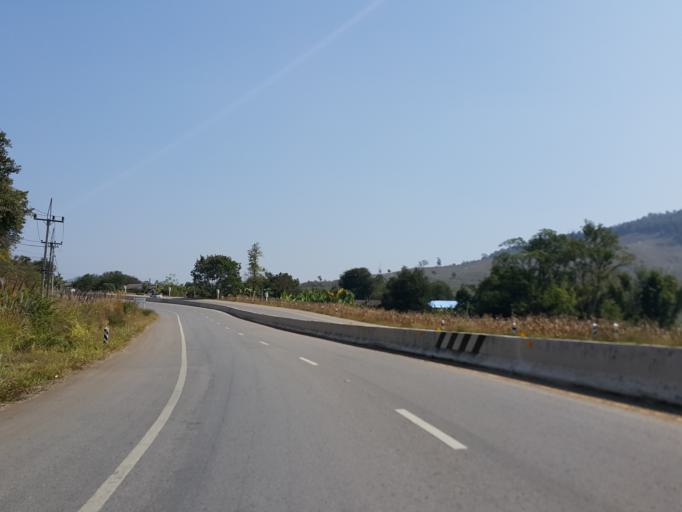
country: TH
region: Lampang
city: Wang Nuea
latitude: 19.1201
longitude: 99.4753
